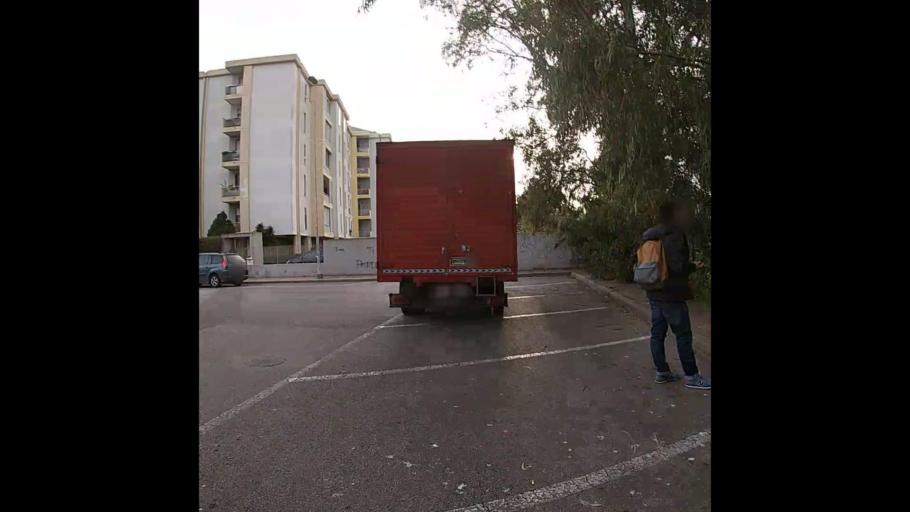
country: IT
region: Sardinia
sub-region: Provincia di Cagliari
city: Su Planu
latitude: 39.2424
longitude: 9.1043
